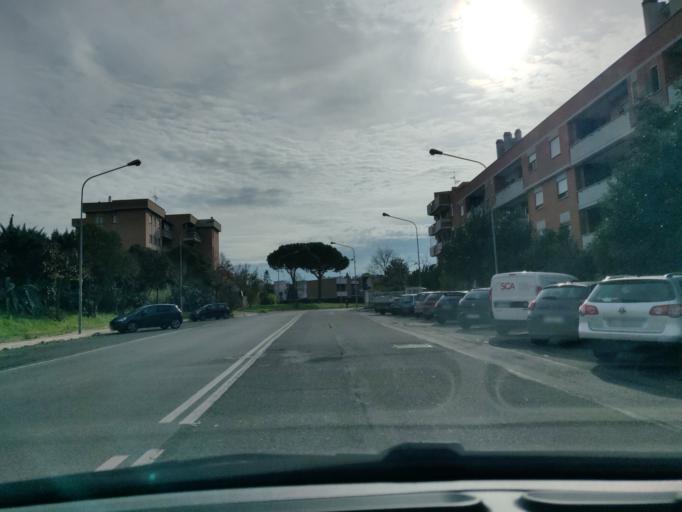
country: IT
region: Latium
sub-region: Citta metropolitana di Roma Capitale
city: Civitavecchia
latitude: 42.1023
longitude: 11.8088
